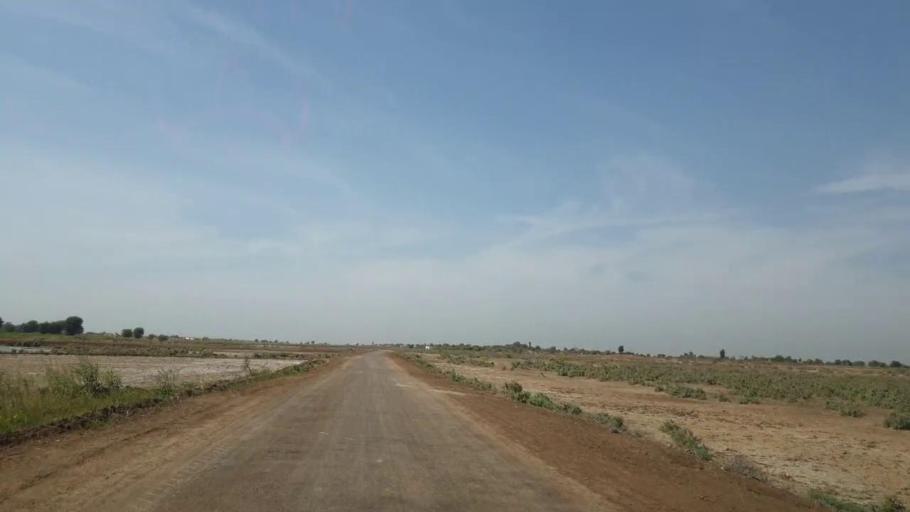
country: PK
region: Sindh
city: Kunri
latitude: 25.2164
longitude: 69.5347
